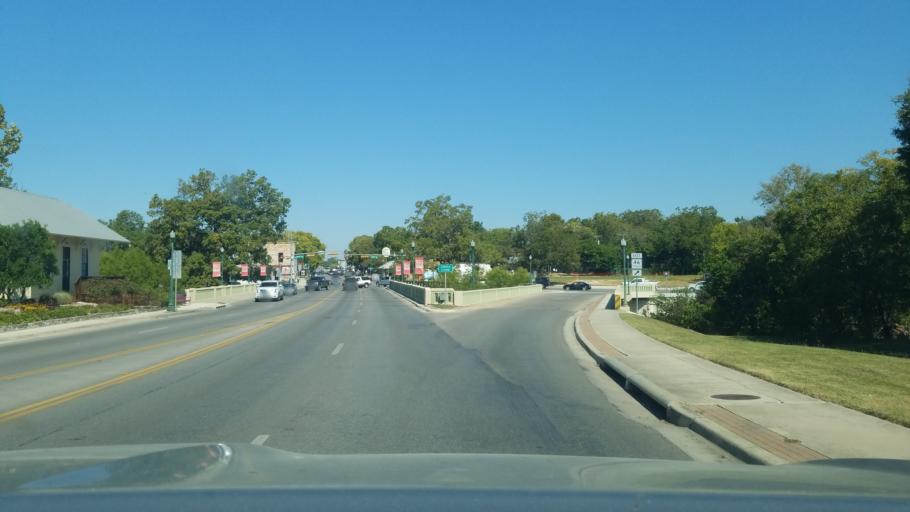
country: US
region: Texas
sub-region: Kendall County
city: Boerne
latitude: 29.7884
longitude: -98.7291
